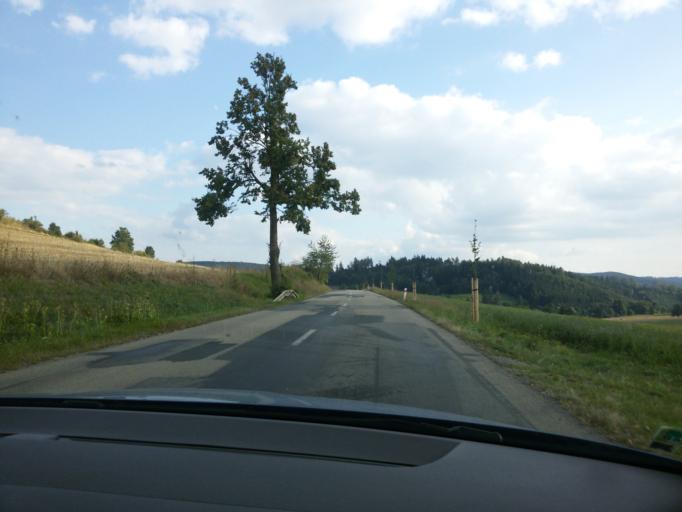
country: CZ
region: South Moravian
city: Olesnice
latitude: 49.5501
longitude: 16.4297
